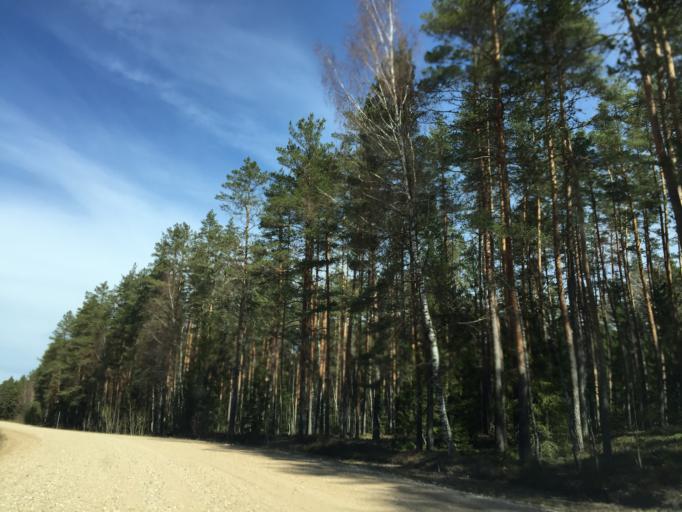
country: LV
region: Strenci
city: Seda
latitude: 57.6333
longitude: 25.8603
